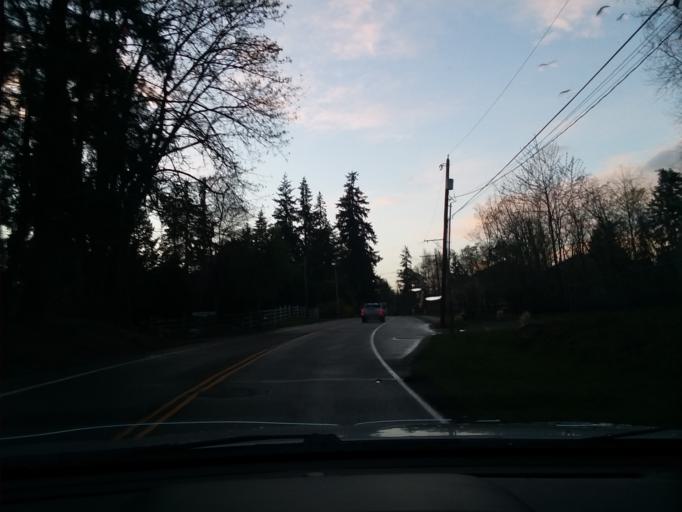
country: US
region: Washington
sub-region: King County
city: Kenmore
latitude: 47.7735
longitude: -122.2443
